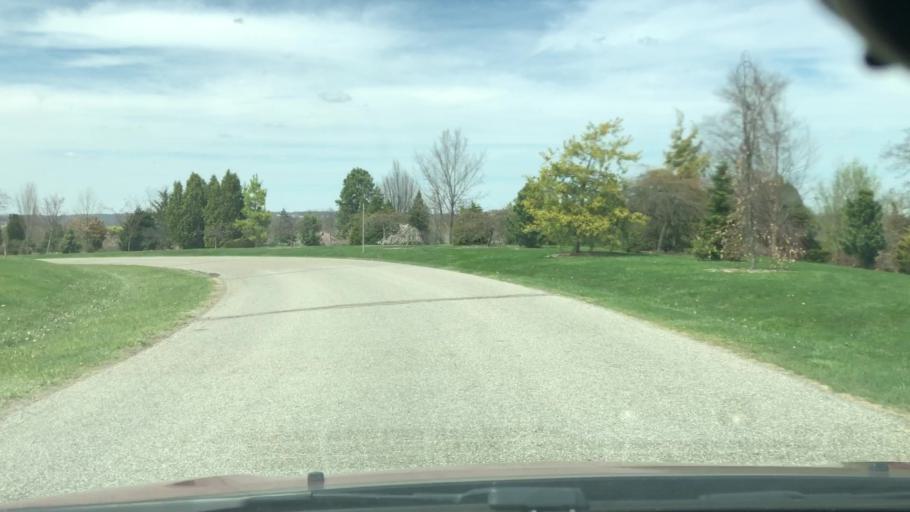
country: US
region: Ohio
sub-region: Wayne County
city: Wooster
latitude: 40.7823
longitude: -81.9169
